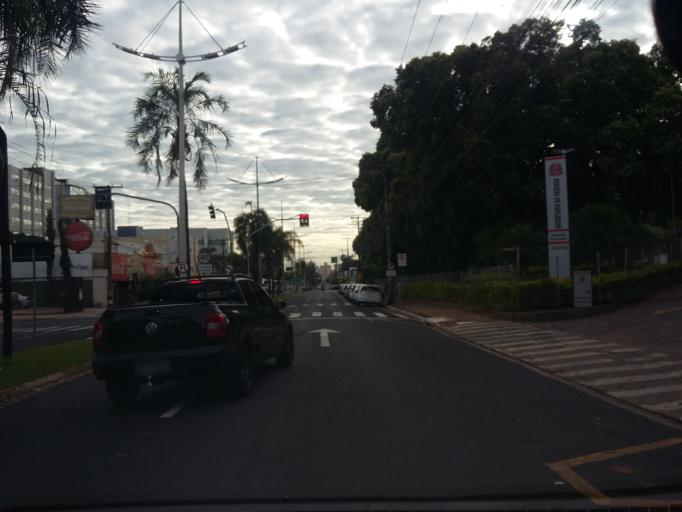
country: BR
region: Sao Paulo
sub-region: Sao Jose Do Rio Preto
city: Sao Jose do Rio Preto
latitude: -20.8305
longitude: -49.3979
